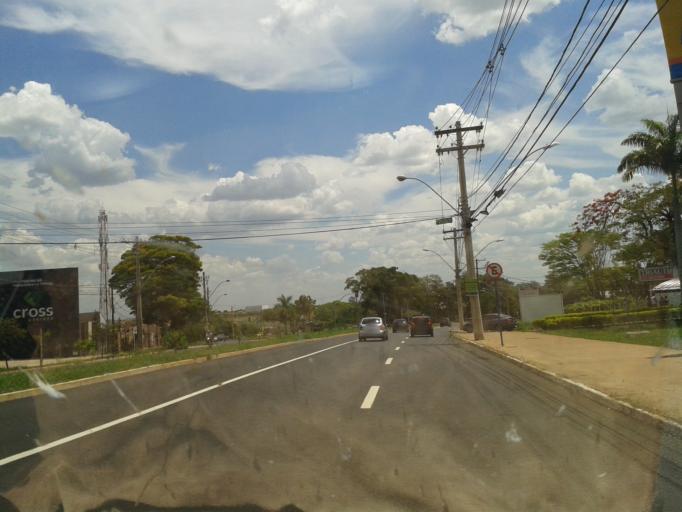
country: BR
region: Minas Gerais
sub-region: Uberaba
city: Uberaba
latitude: -19.7496
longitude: -47.9755
